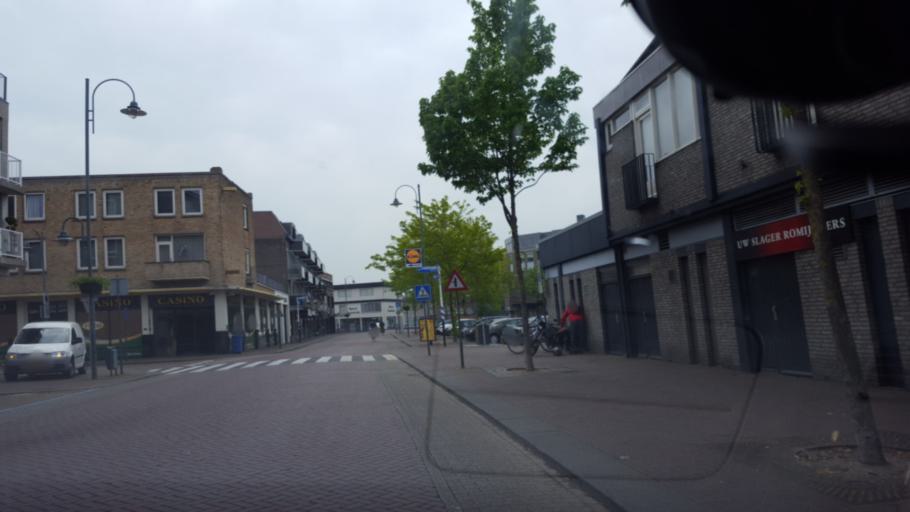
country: NL
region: North Brabant
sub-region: Gemeente Veghel
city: Veghel
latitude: 51.6170
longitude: 5.5464
